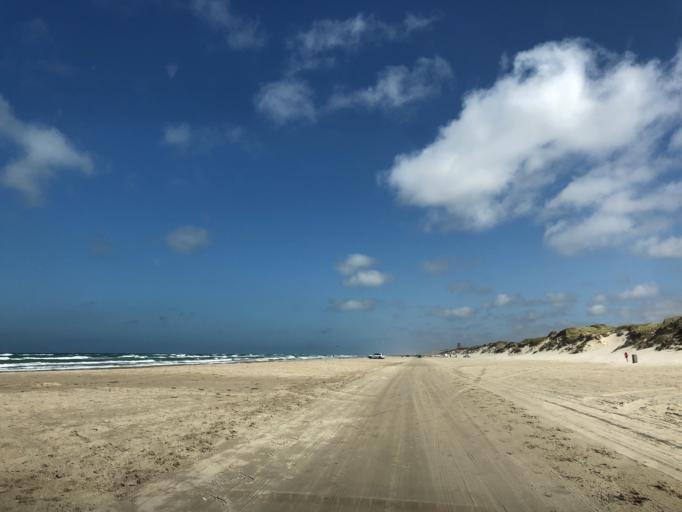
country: DK
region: North Denmark
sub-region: Jammerbugt Kommune
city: Pandrup
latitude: 57.2469
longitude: 9.5690
